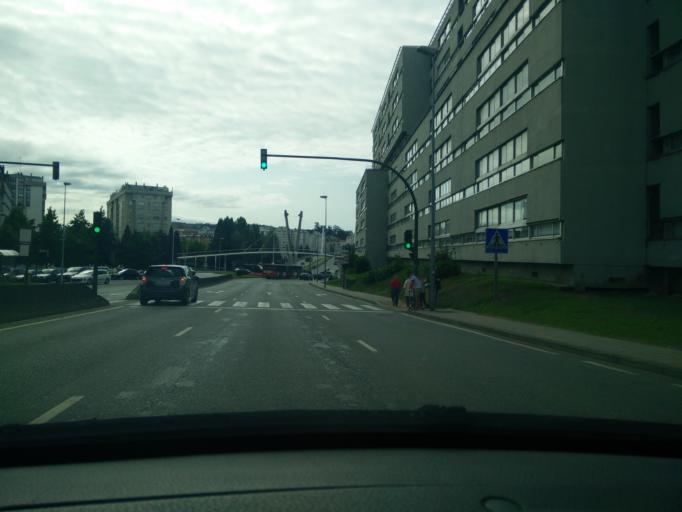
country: ES
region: Galicia
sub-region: Provincia da Coruna
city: A Coruna
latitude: 43.3429
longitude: -8.4033
